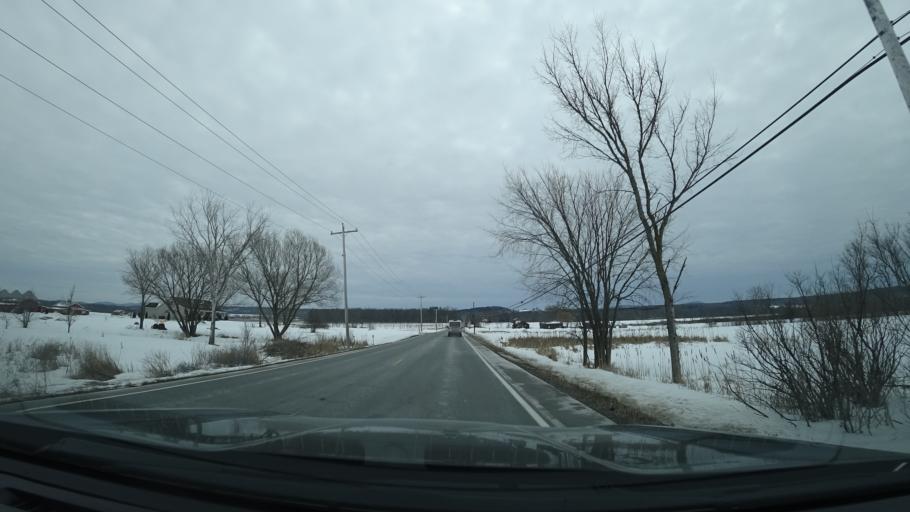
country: US
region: New York
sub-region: Washington County
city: Fort Edward
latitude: 43.2638
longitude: -73.5363
